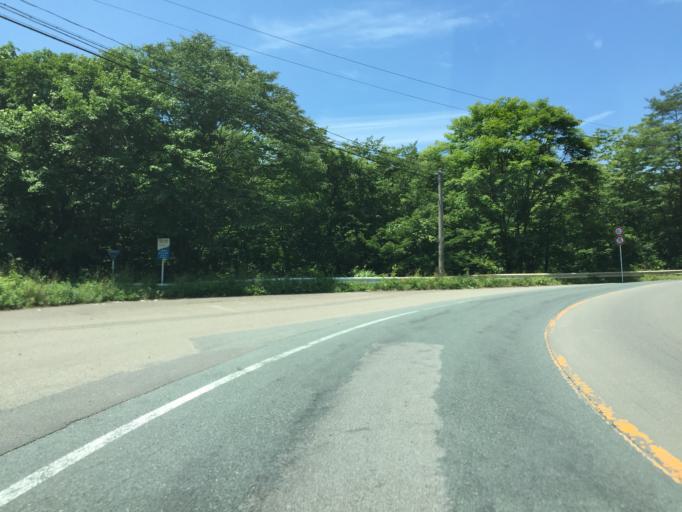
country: JP
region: Miyagi
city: Marumori
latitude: 37.7709
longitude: 140.7700
